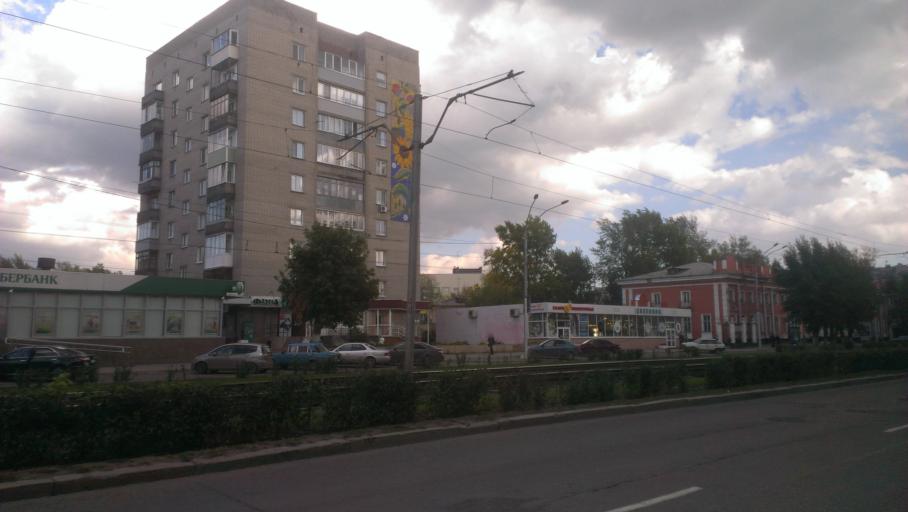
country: RU
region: Altai Krai
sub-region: Gorod Barnaulskiy
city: Barnaul
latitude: 53.3595
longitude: 83.7645
